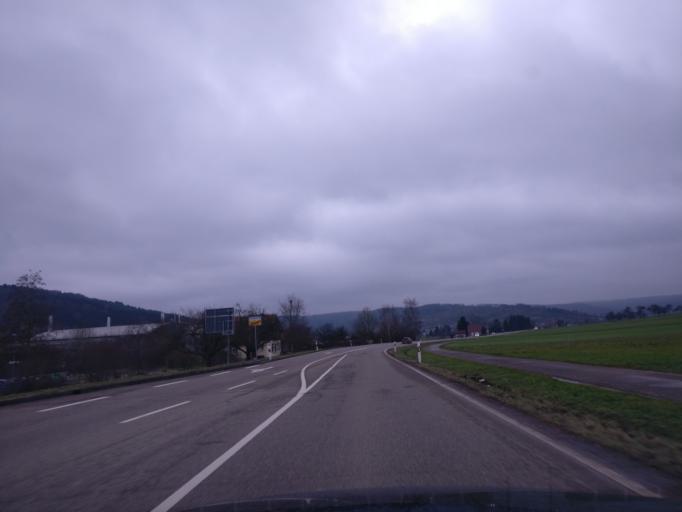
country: DE
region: Baden-Wuerttemberg
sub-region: Regierungsbezirk Stuttgart
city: Rudersberg
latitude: 48.8619
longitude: 9.5365
